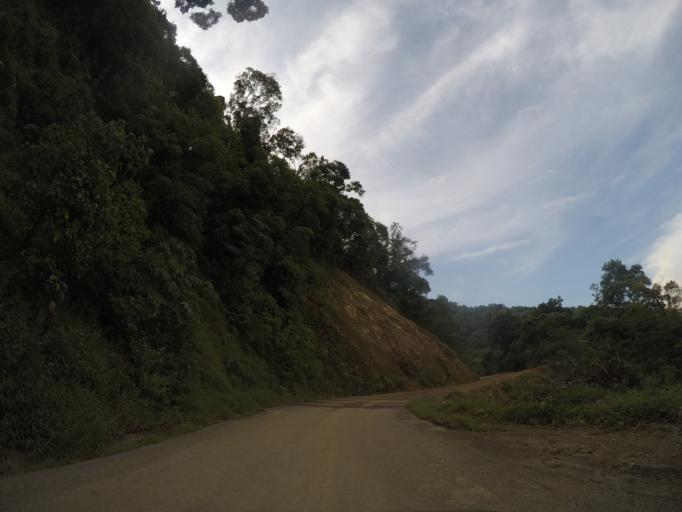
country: MX
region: Oaxaca
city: Pluma Hidalgo
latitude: 15.9492
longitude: -96.4406
